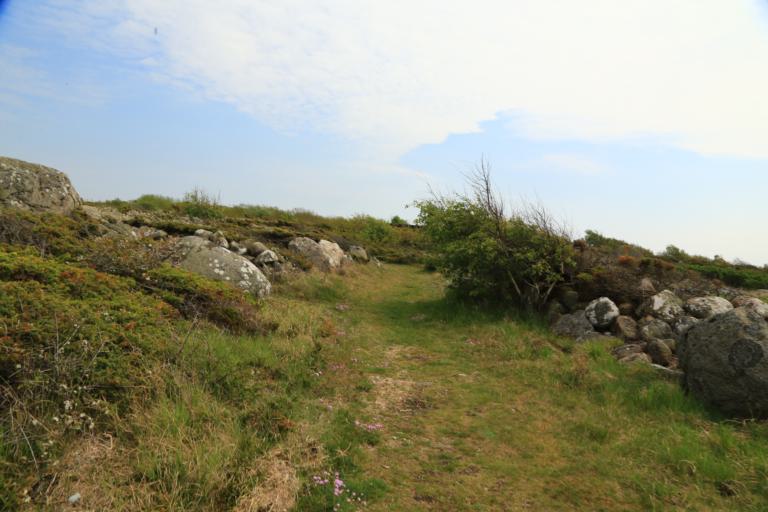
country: SE
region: Halland
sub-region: Varbergs Kommun
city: Varberg
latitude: 57.1517
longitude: 12.2089
